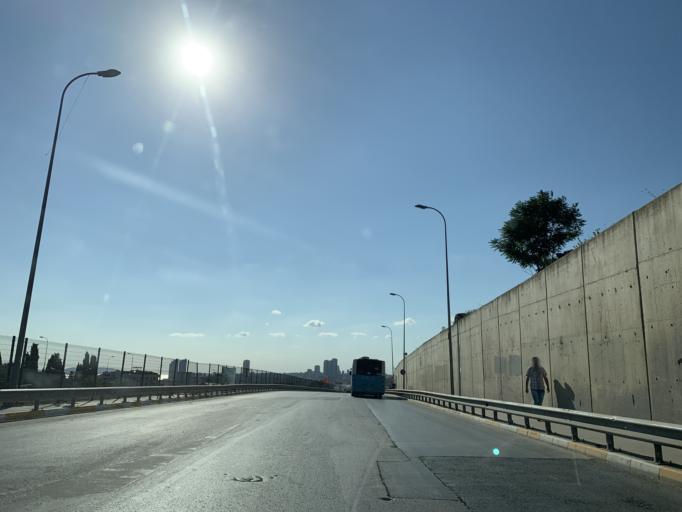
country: TR
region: Istanbul
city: Pendik
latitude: 40.8816
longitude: 29.2504
